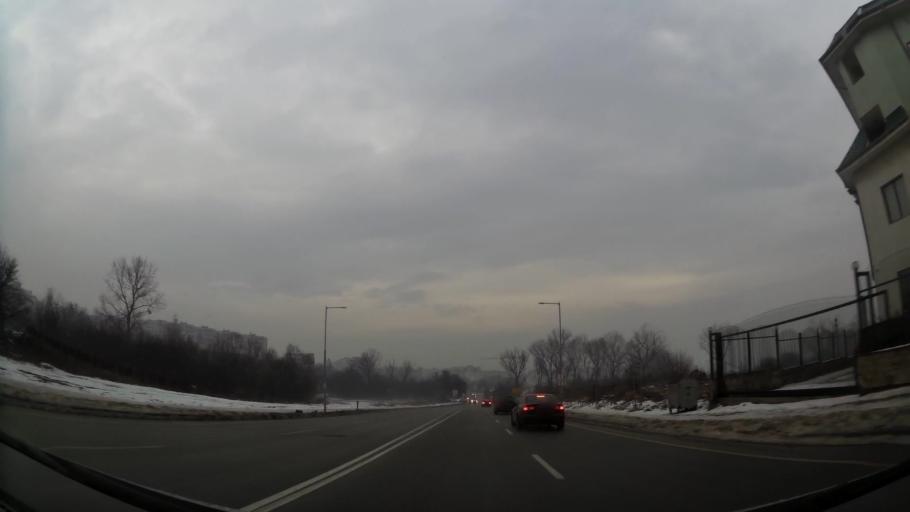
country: BG
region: Sofia-Capital
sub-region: Stolichna Obshtina
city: Sofia
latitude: 42.6815
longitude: 23.2552
